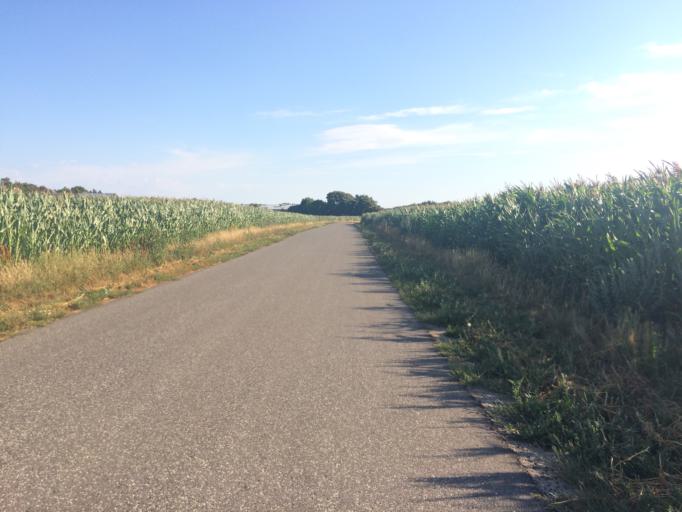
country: DK
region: Central Jutland
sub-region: Holstebro Kommune
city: Vinderup
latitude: 56.6103
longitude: 8.7744
